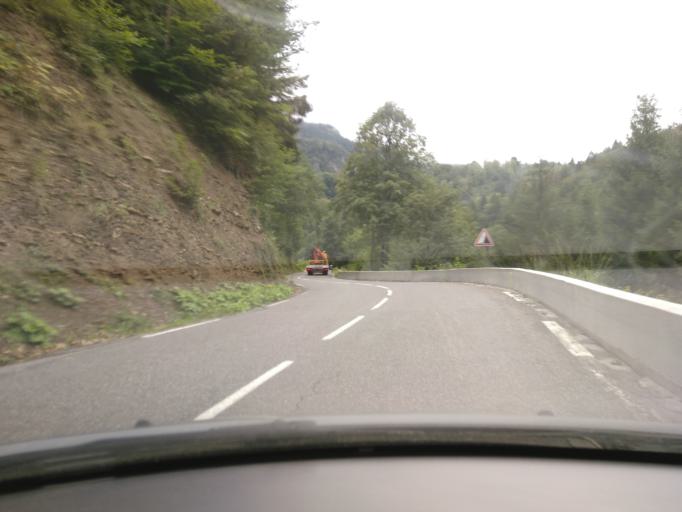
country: FR
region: Rhone-Alpes
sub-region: Departement de la Haute-Savoie
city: Bonneville
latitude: 46.0497
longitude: 6.3764
